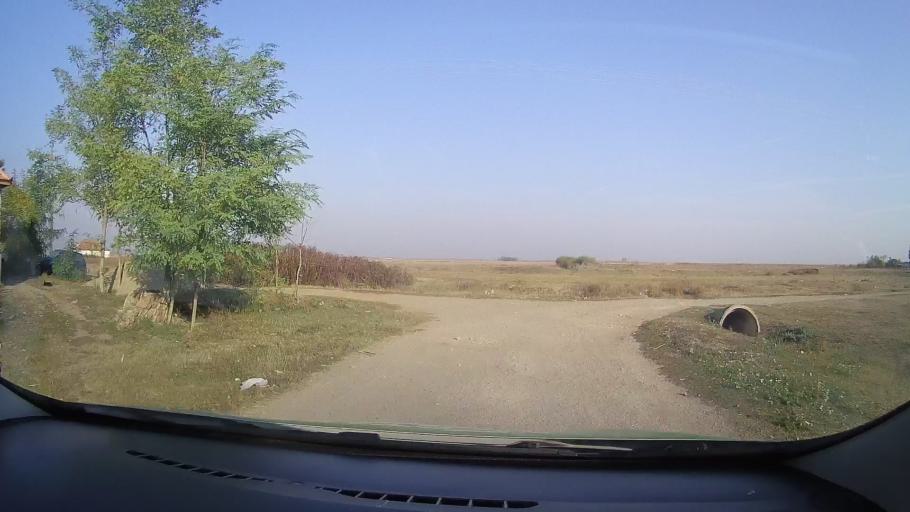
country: RO
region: Arad
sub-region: Comuna Graniceri
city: Graniceri
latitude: 46.5273
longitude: 21.3097
